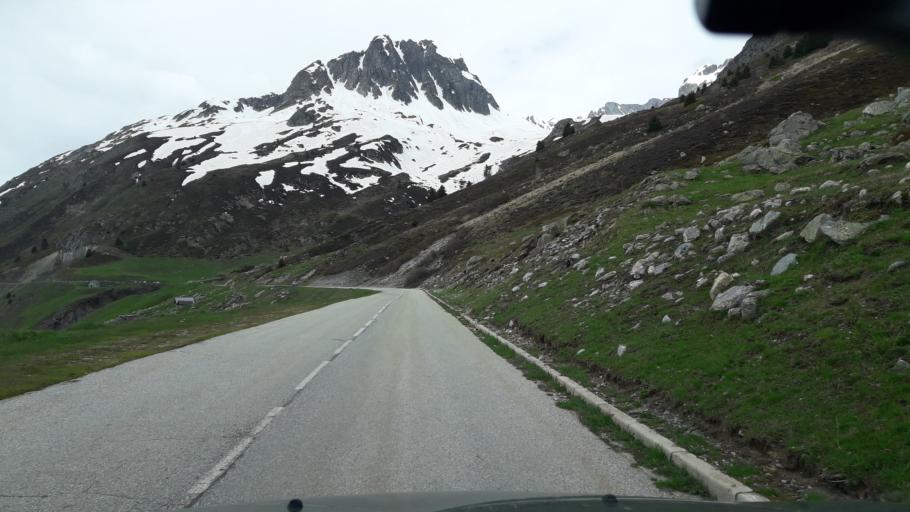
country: FR
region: Rhone-Alpes
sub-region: Departement de l'Isere
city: Huez
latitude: 45.2265
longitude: 6.1472
